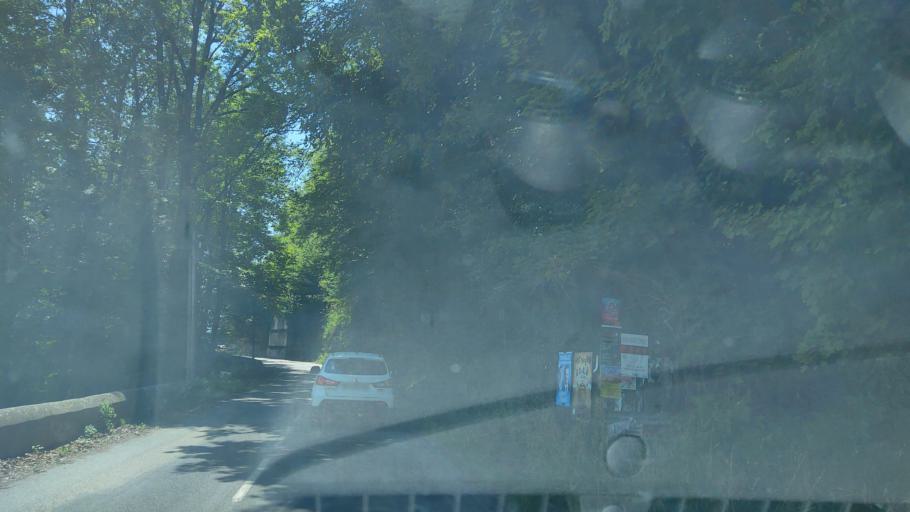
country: FR
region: Rhone-Alpes
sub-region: Departement de la Savoie
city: Aiton
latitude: 45.5162
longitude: 6.3031
